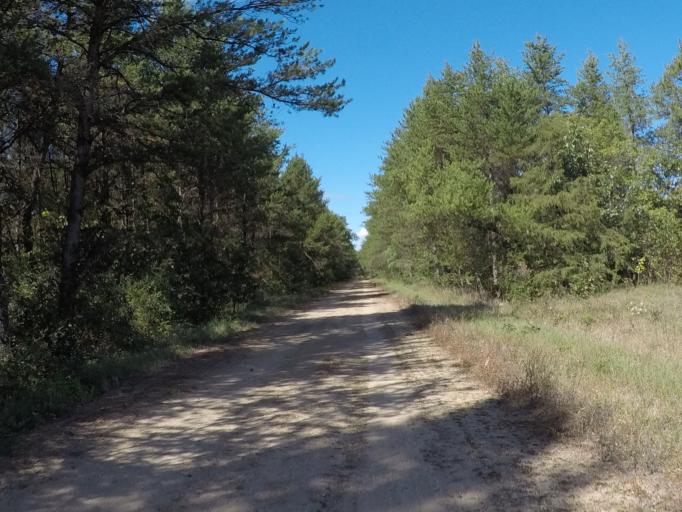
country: US
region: Wisconsin
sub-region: Richland County
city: Richland Center
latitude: 43.2170
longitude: -90.2880
